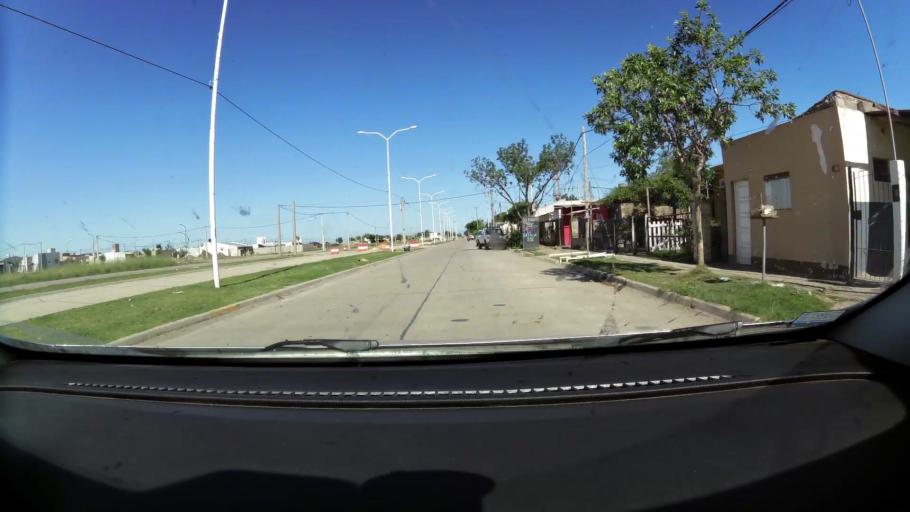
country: AR
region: Santa Fe
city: Rafaela
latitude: -31.2357
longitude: -61.4779
